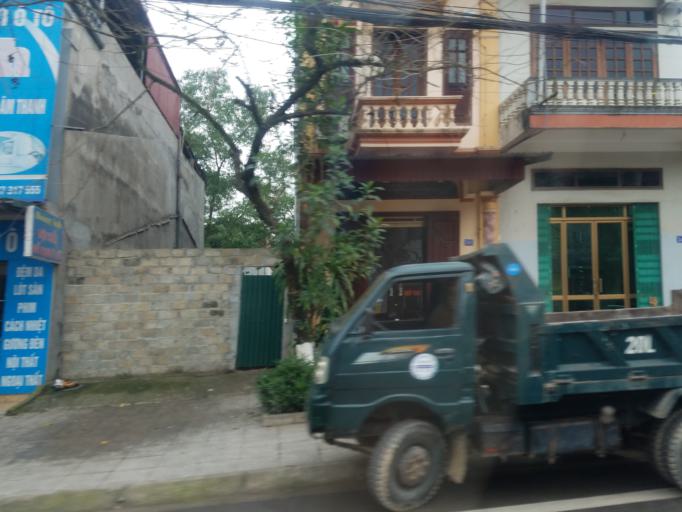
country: VN
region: Thai Nguyen
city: Thanh Pho Thai Nguyen
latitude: 21.5840
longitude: 105.8393
